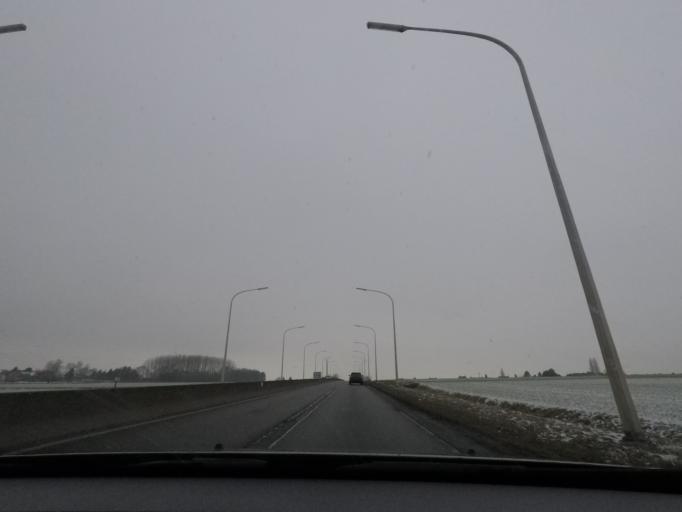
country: BE
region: Wallonia
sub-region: Province du Hainaut
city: Aiseau
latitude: 50.4654
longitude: 4.6315
